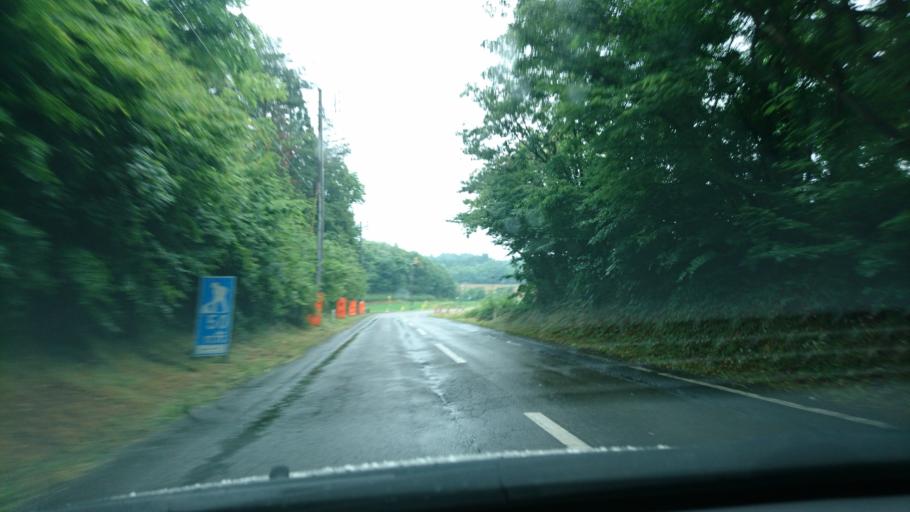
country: JP
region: Iwate
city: Ichinoseki
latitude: 38.9157
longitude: 141.0295
